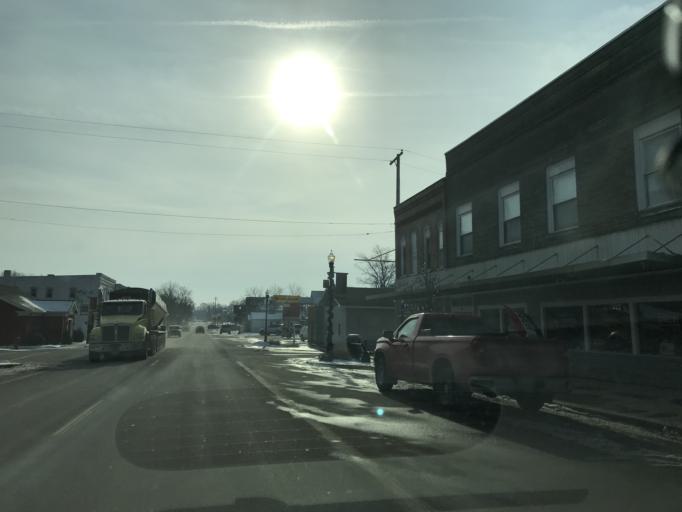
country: US
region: Michigan
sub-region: Barry County
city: Nashville
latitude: 42.6038
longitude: -85.0936
